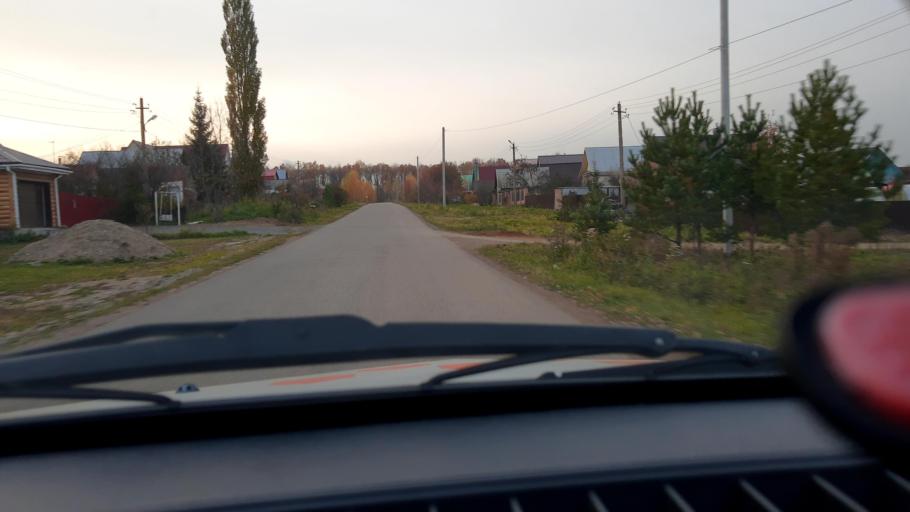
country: RU
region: Bashkortostan
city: Iglino
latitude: 54.7949
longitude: 56.3166
